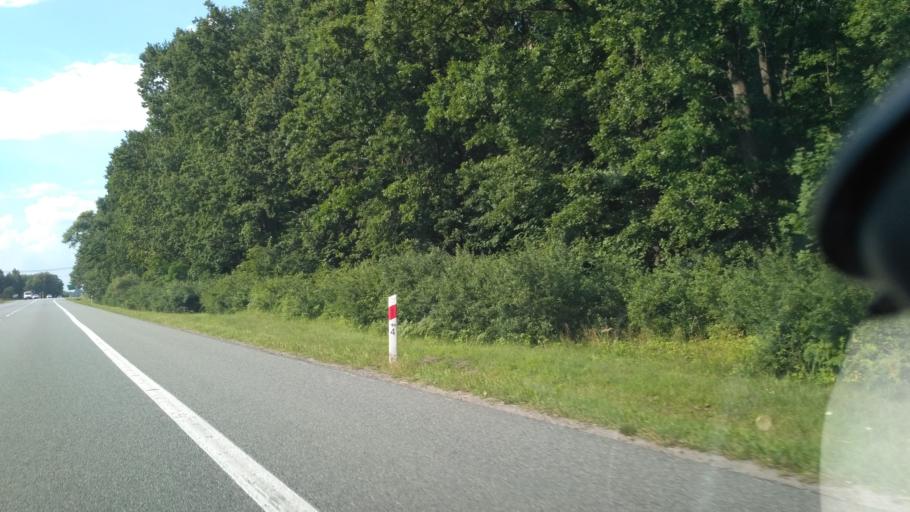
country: PL
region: Subcarpathian Voivodeship
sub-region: Powiat rzeszowski
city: Glogow Malopolski
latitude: 50.1306
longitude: 21.9672
